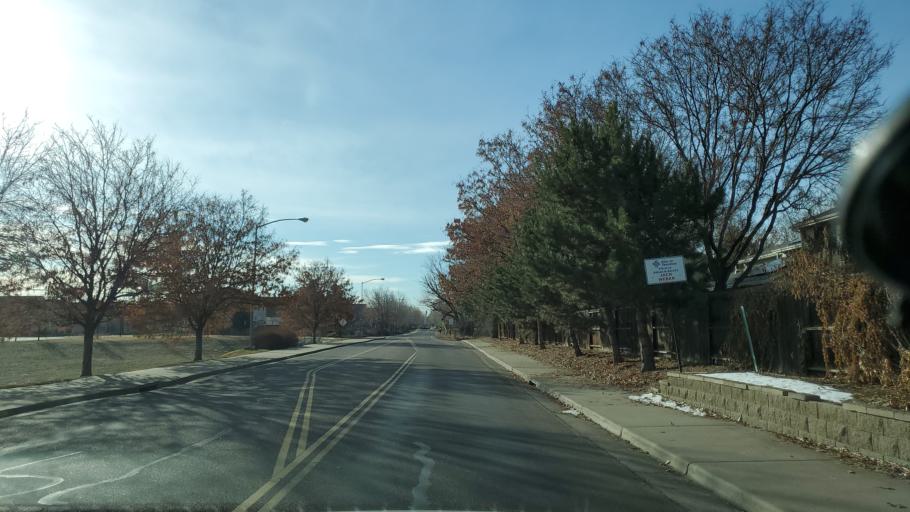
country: US
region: Colorado
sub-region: Adams County
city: Northglenn
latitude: 39.9208
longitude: -104.9497
